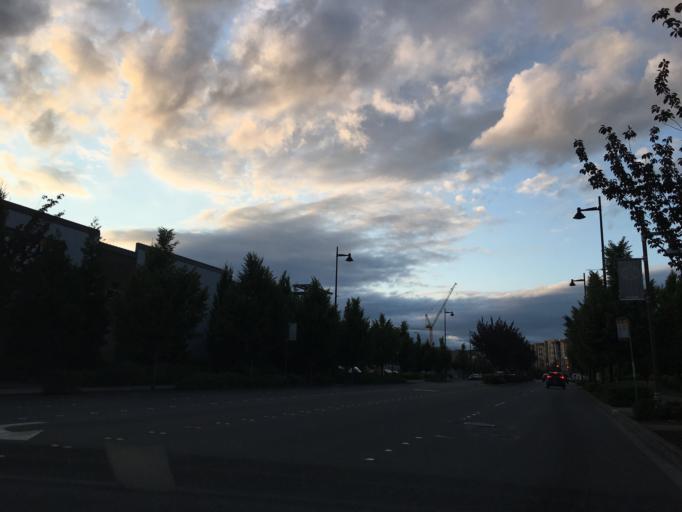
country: US
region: Washington
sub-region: King County
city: Renton
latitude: 47.4959
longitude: -122.2018
